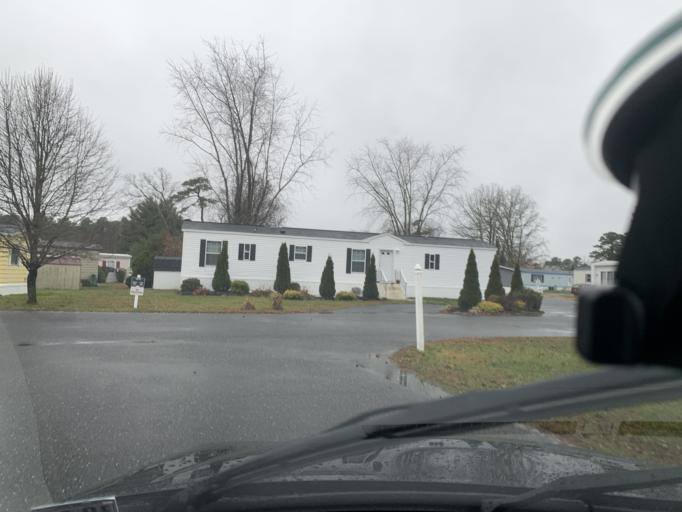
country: US
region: New Jersey
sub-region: Atlantic County
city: Pomona
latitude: 39.4364
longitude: -74.5970
